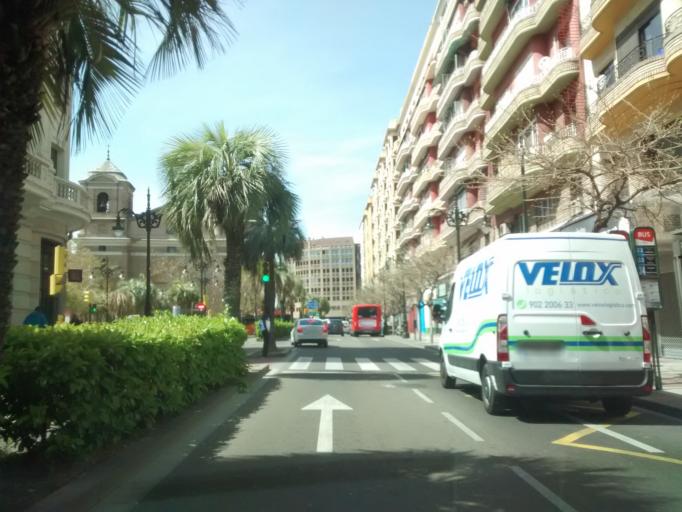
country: ES
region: Aragon
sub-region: Provincia de Zaragoza
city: Almozara
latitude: 41.6559
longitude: -0.8916
